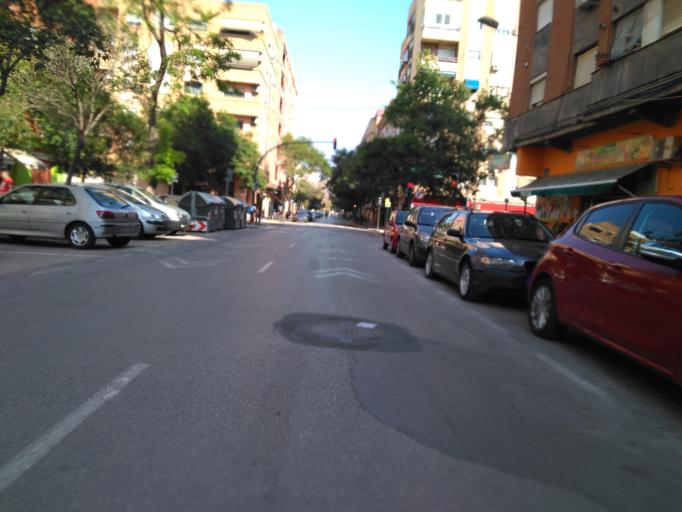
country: ES
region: Valencia
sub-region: Provincia de Valencia
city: Tavernes Blanques
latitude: 39.4927
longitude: -0.3895
